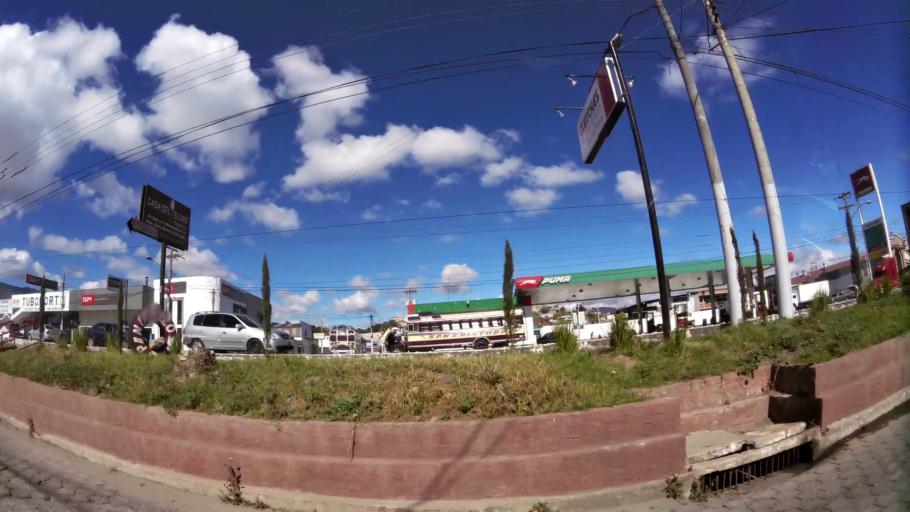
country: GT
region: Quetzaltenango
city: Quetzaltenango
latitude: 14.8357
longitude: -91.5106
